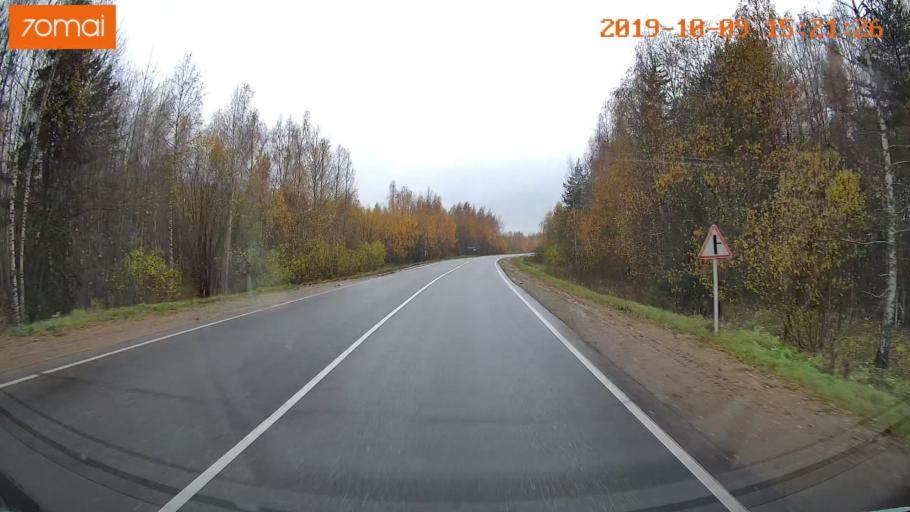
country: RU
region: Kostroma
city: Susanino
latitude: 58.0535
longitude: 41.5197
